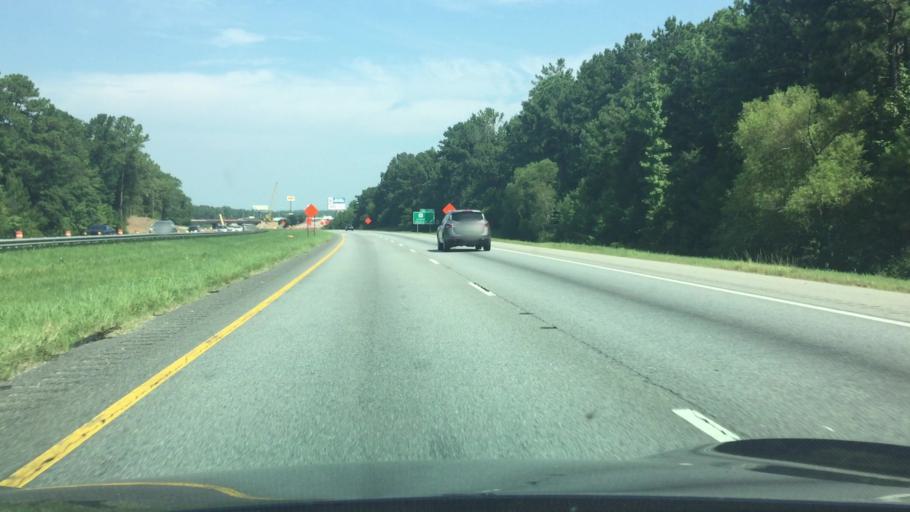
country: US
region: Alabama
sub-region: Shelby County
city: Calera
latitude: 33.1371
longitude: -86.7452
